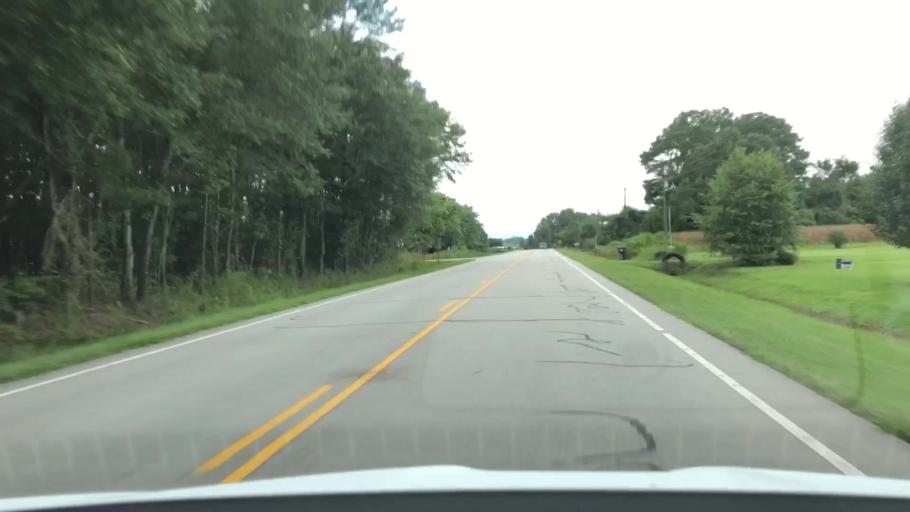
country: US
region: North Carolina
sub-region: Lenoir County
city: Kinston
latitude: 35.1345
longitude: -77.5268
